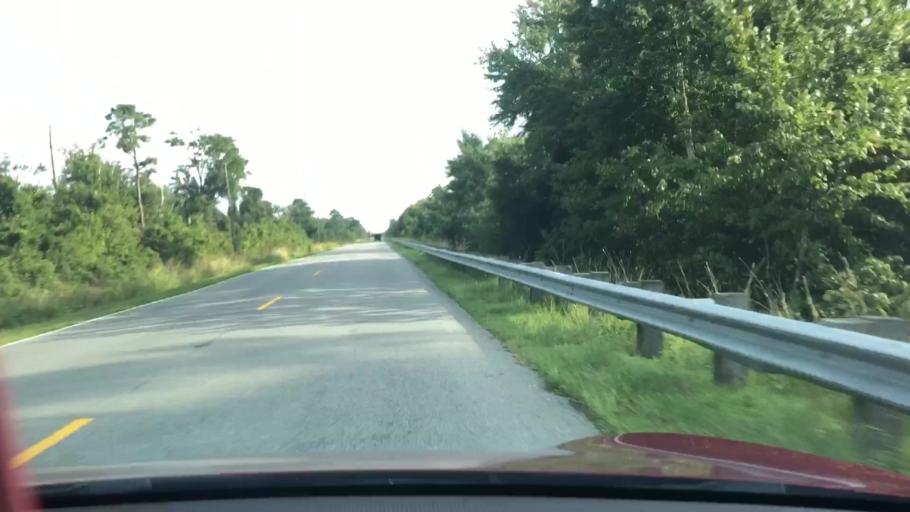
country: US
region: North Carolina
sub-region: Dare County
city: Wanchese
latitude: 35.7175
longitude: -75.7684
